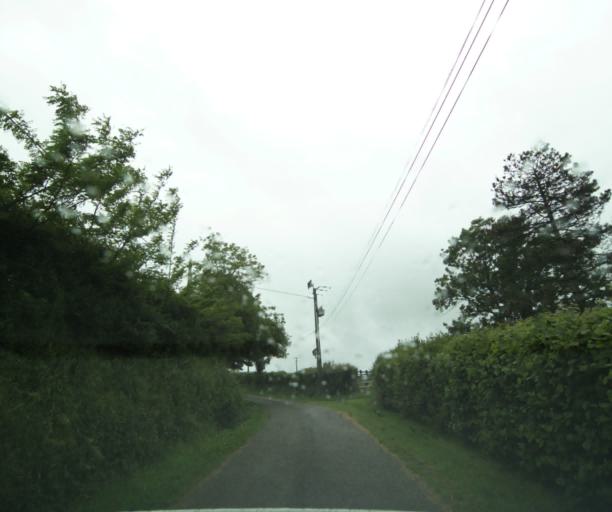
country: FR
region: Bourgogne
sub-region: Departement de Saone-et-Loire
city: Matour
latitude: 46.4859
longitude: 4.4656
